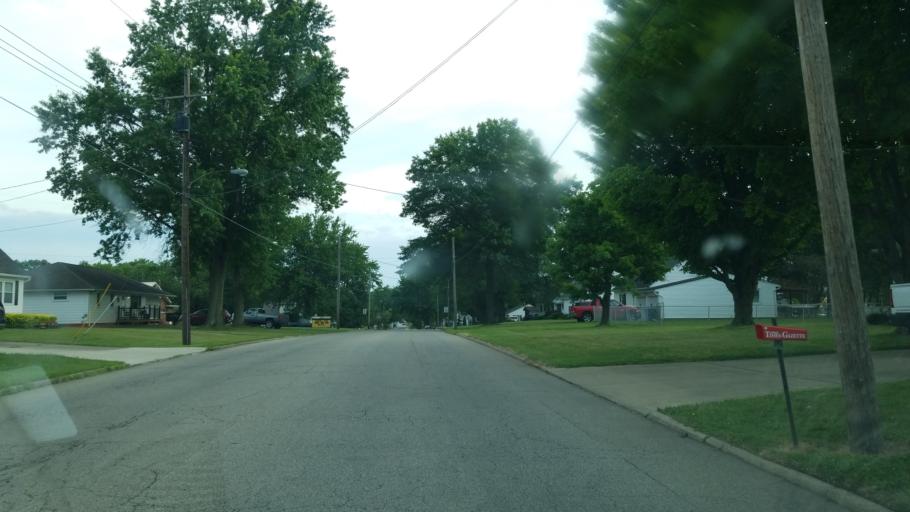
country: US
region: Ohio
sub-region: Ashland County
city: Ashland
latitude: 40.8601
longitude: -82.2963
